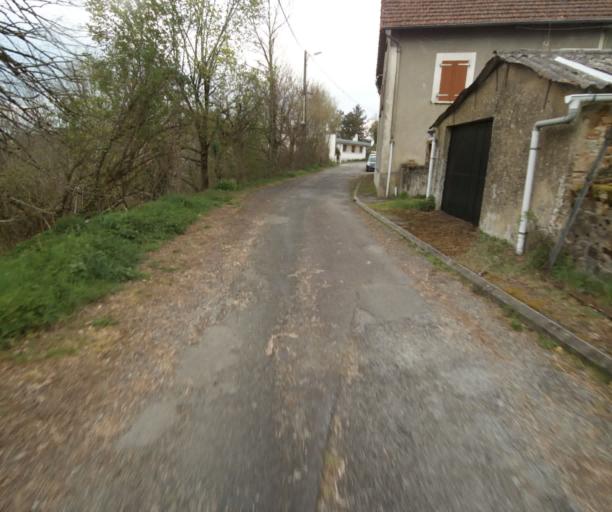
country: FR
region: Limousin
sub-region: Departement de la Correze
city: Tulle
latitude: 45.2568
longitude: 1.7649
